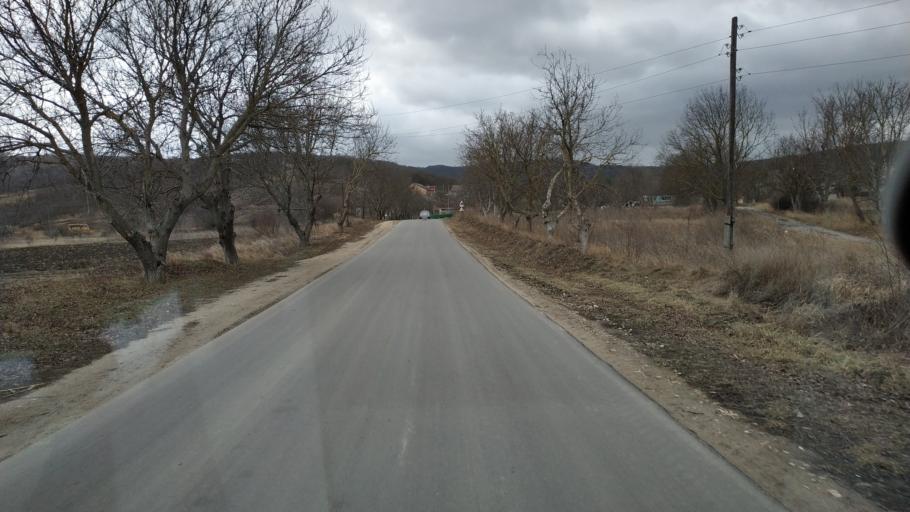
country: MD
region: Calarasi
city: Calarasi
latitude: 47.2482
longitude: 28.2866
